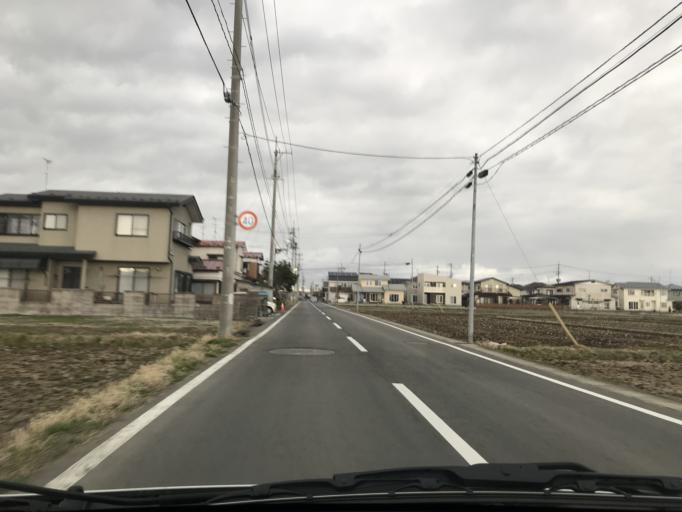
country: JP
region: Iwate
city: Mizusawa
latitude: 39.1305
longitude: 141.1605
